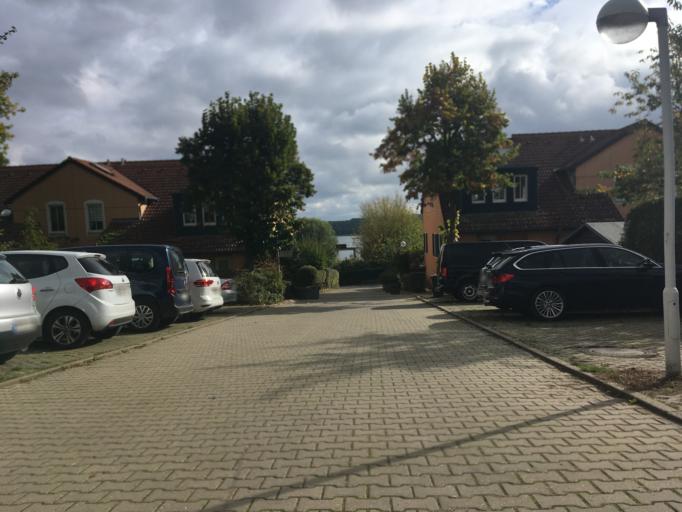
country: DE
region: Berlin
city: Kladow
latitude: 52.4465
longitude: 13.1315
